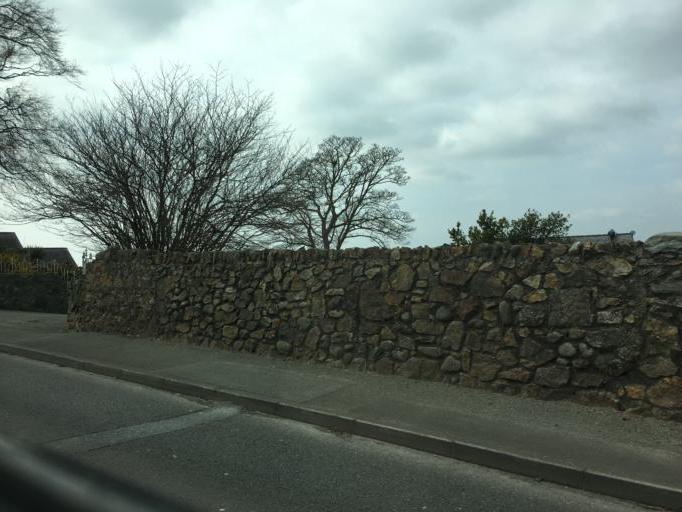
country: GB
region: Wales
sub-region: Gwynedd
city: Caernarfon
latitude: 53.1497
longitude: -4.2649
